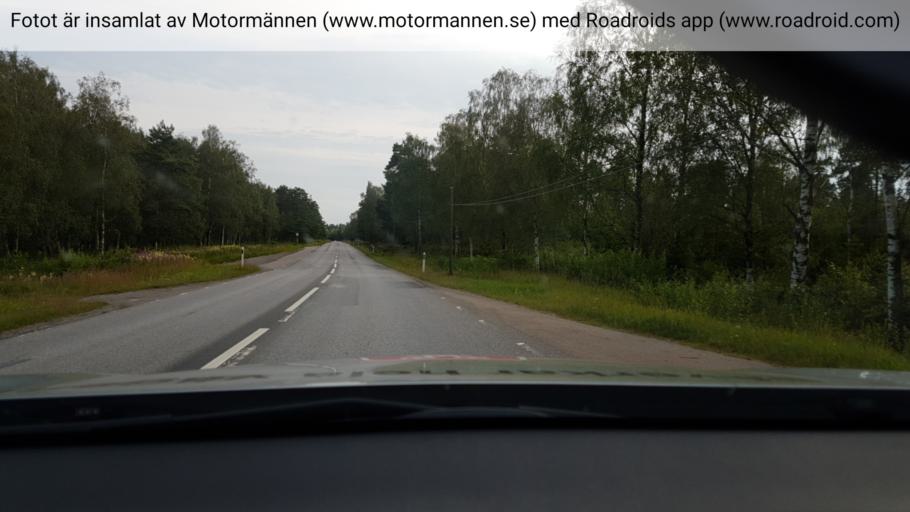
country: SE
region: Vaestra Goetaland
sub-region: Uddevalla Kommun
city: Uddevalla
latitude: 58.3734
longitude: 11.9760
